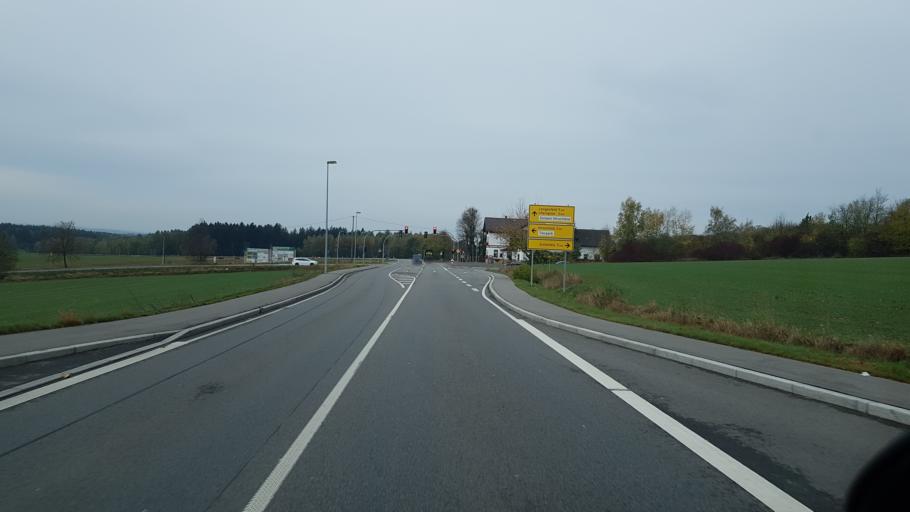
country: DE
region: Saxony
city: Hirschfeld
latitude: 50.6353
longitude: 12.4352
